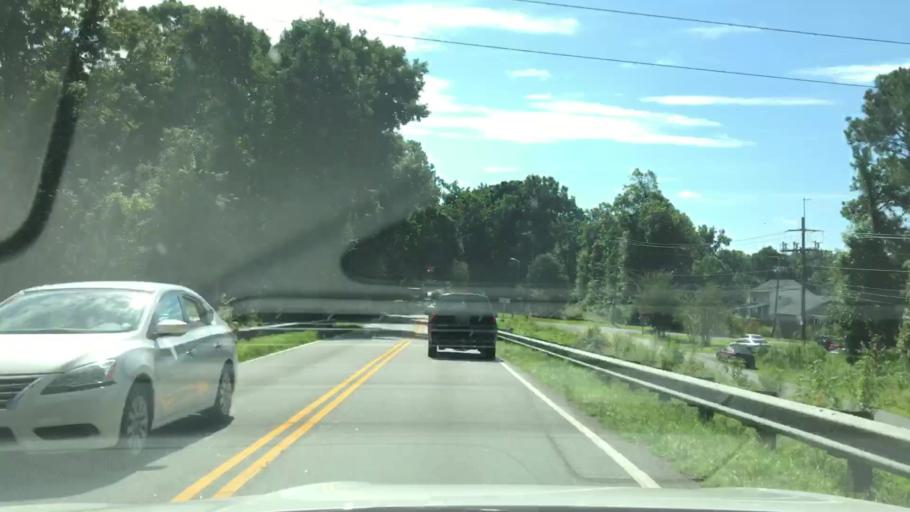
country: US
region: South Carolina
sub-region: Charleston County
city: Shell Point
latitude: 32.8404
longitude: -80.0543
